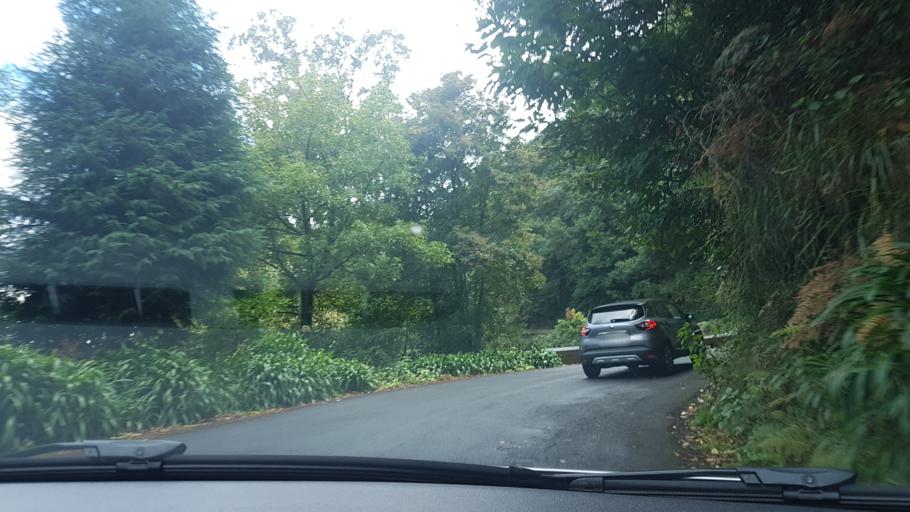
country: PT
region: Madeira
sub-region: Sao Vicente
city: Sao Vicente
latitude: 32.7635
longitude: -17.0257
